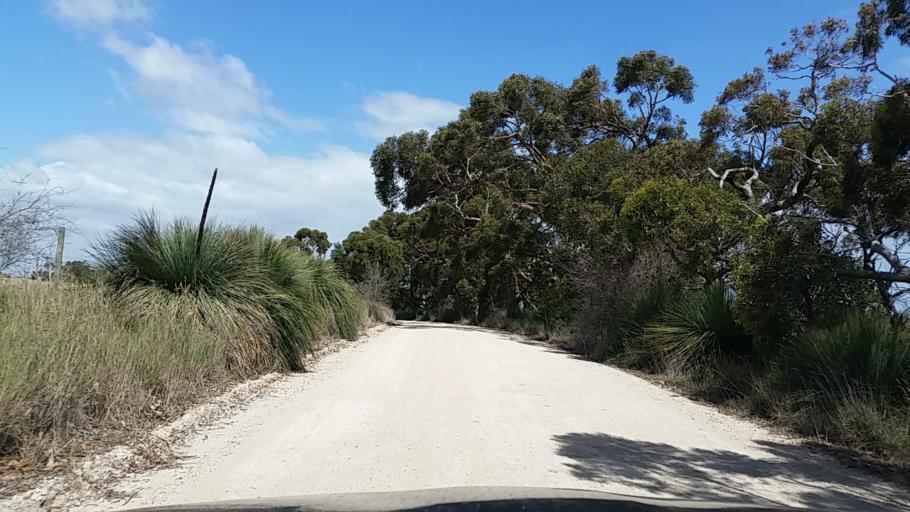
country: AU
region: South Australia
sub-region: Alexandrina
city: Port Elliot
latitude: -35.4501
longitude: 138.6513
